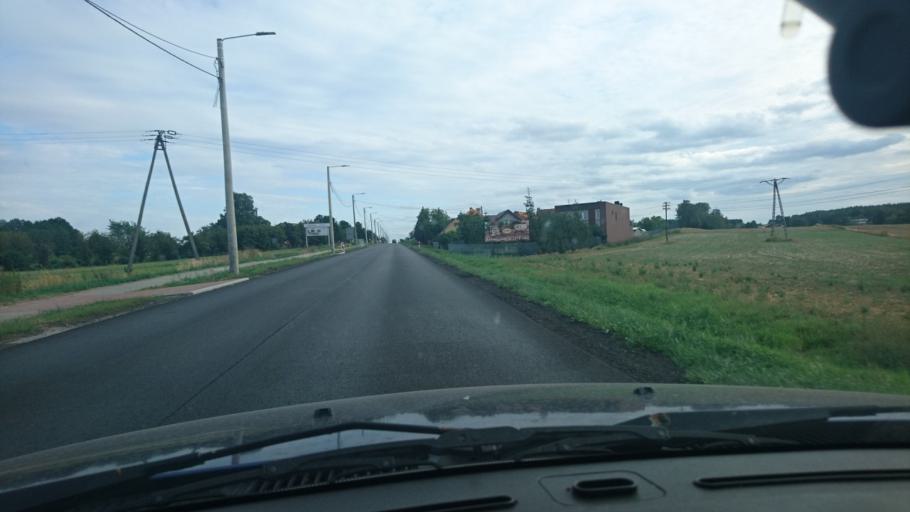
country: PL
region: Greater Poland Voivodeship
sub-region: Powiat ostrzeszowski
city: Ostrzeszow
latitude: 51.4116
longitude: 17.9337
